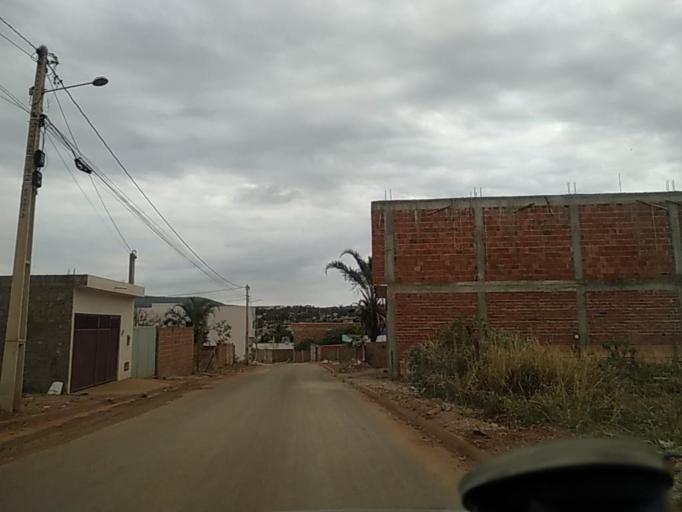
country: BR
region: Bahia
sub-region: Caetite
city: Caetite
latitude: -14.0509
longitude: -42.4743
